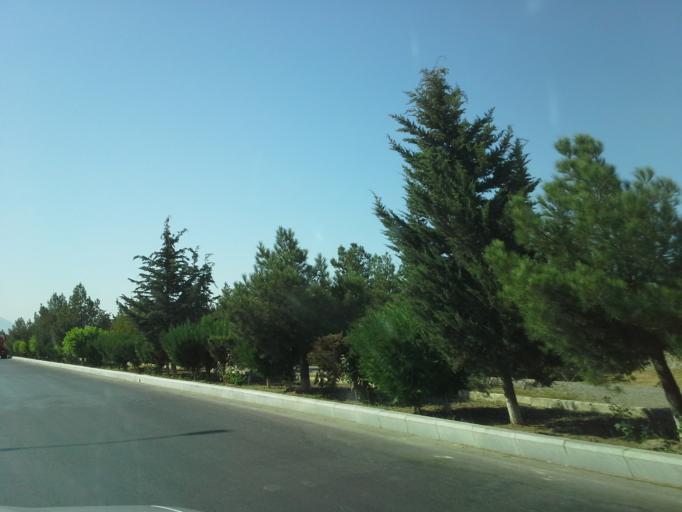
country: TM
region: Ahal
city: Annau
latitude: 37.9188
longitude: 58.4560
